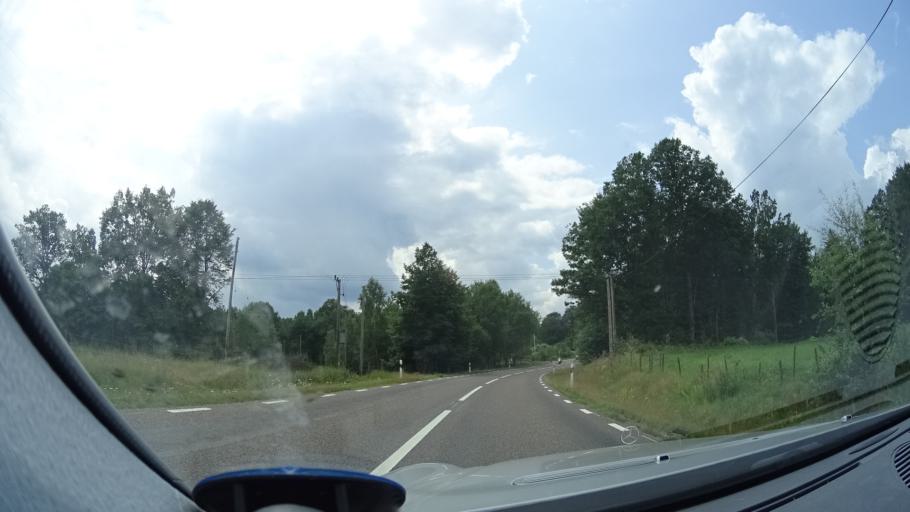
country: SE
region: Kalmar
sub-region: Emmaboda Kommun
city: Emmaboda
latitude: 56.6307
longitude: 15.6466
